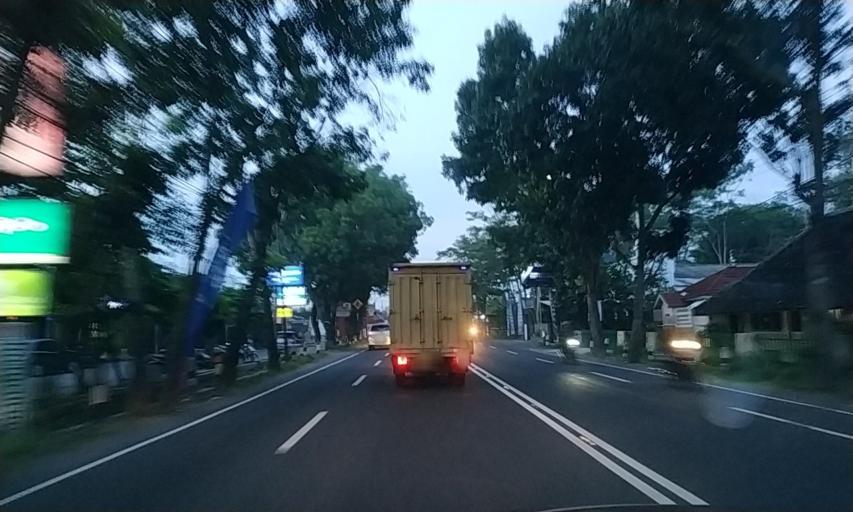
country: ID
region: Daerah Istimewa Yogyakarta
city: Godean
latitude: -7.8360
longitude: 110.2200
